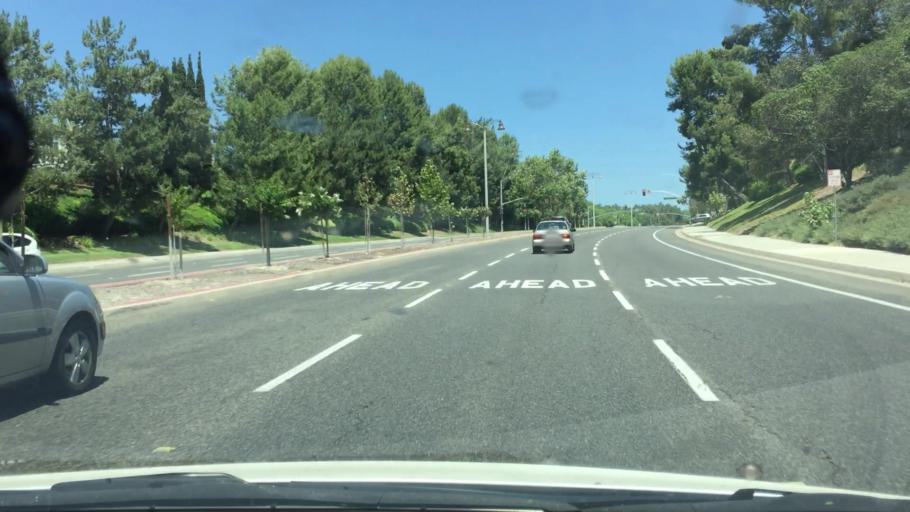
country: US
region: California
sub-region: Orange County
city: Rancho Santa Margarita
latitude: 33.6275
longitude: -117.6375
